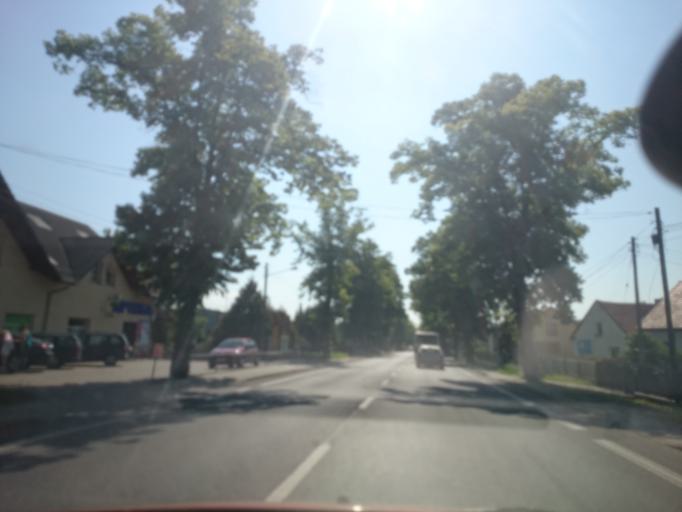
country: PL
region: Opole Voivodeship
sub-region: Powiat opolski
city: Opole
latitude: 50.6458
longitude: 17.9845
